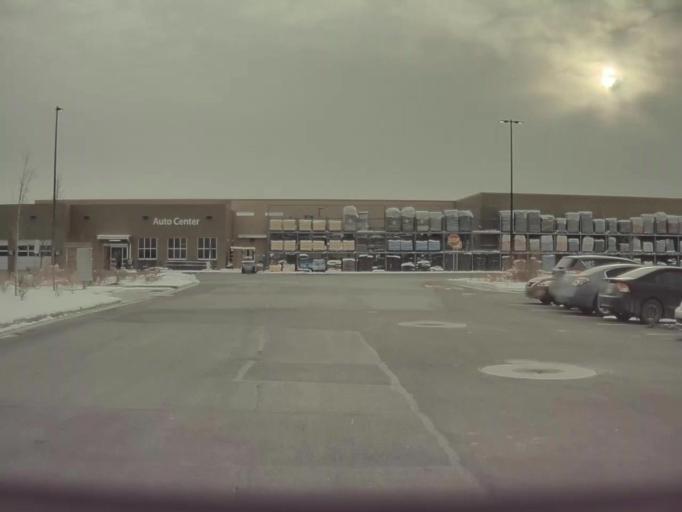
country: US
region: Utah
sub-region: Utah County
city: Spanish Fork
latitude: 40.1247
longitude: -111.6375
